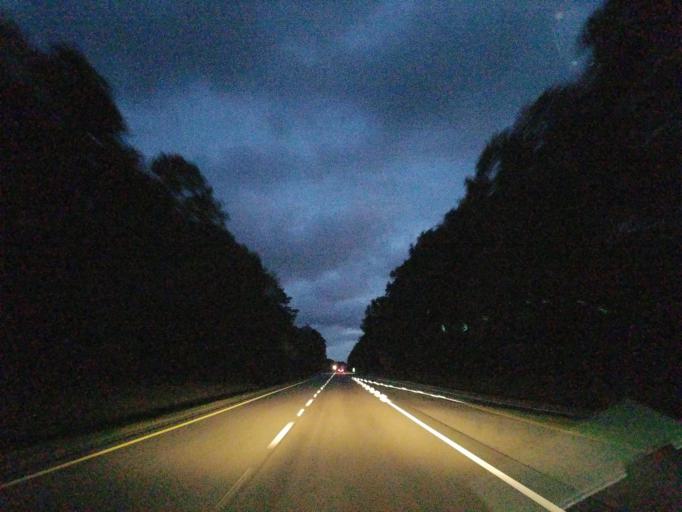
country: US
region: Mississippi
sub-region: Jones County
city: Sharon
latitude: 31.8486
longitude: -89.0492
